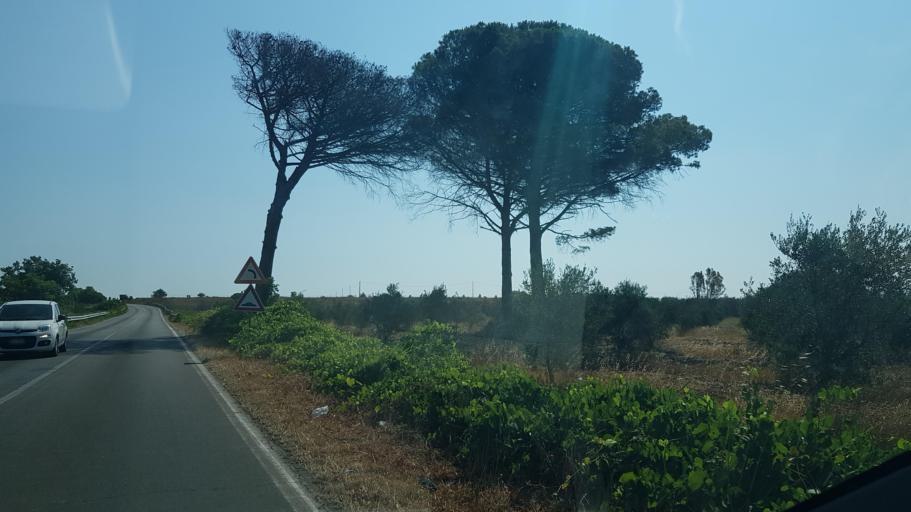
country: IT
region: Apulia
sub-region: Provincia di Lecce
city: Montesano Salentino
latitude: 40.0073
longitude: 18.3142
